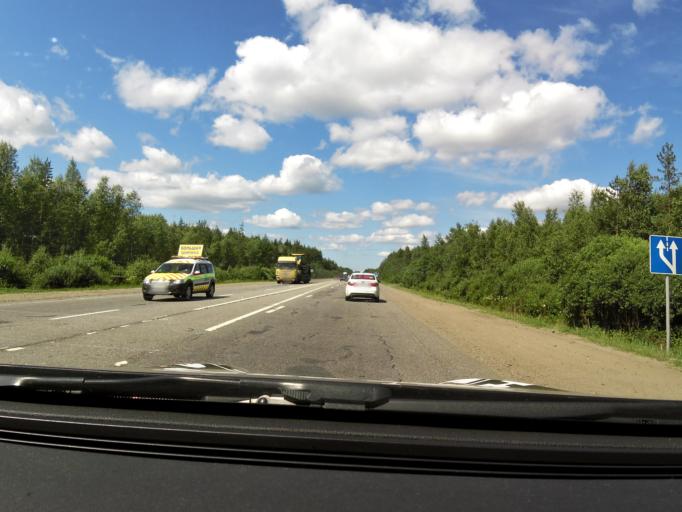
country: RU
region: Tverskaya
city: Kuzhenkino
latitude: 57.7334
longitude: 34.0444
